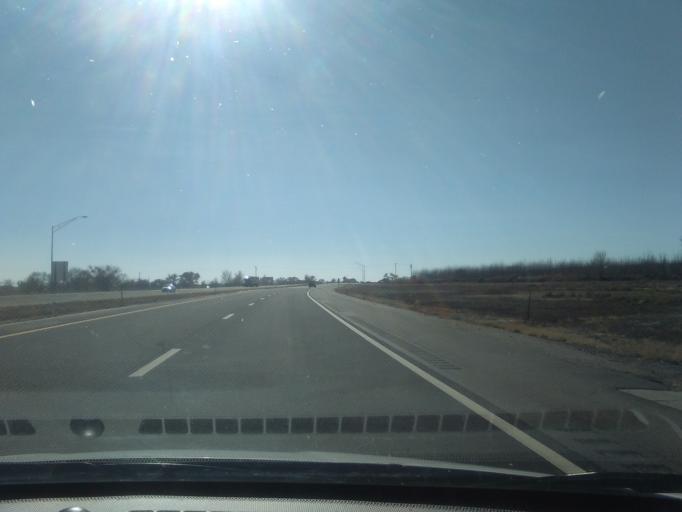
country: US
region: New Mexico
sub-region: Valencia County
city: Jarales
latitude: 34.6296
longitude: -106.7829
